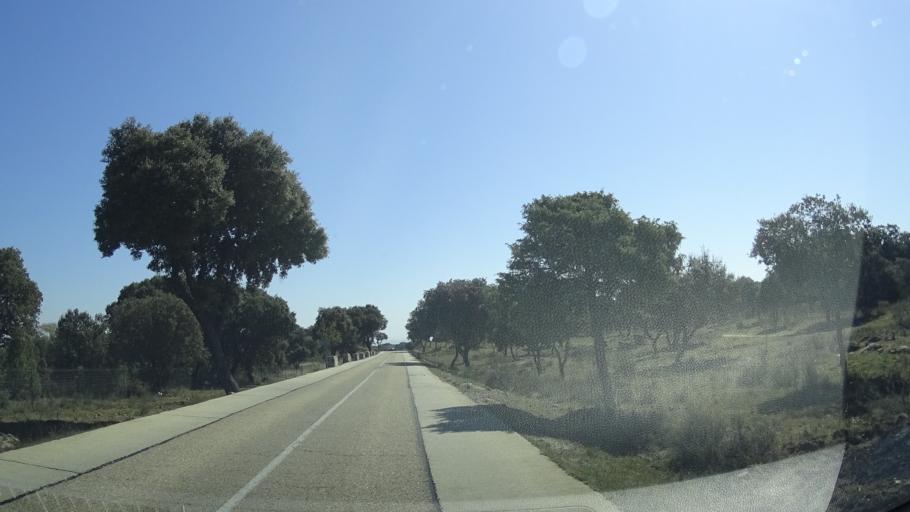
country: ES
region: Madrid
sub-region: Provincia de Madrid
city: Hoyo de Manzanares
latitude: 40.6448
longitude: -3.8388
